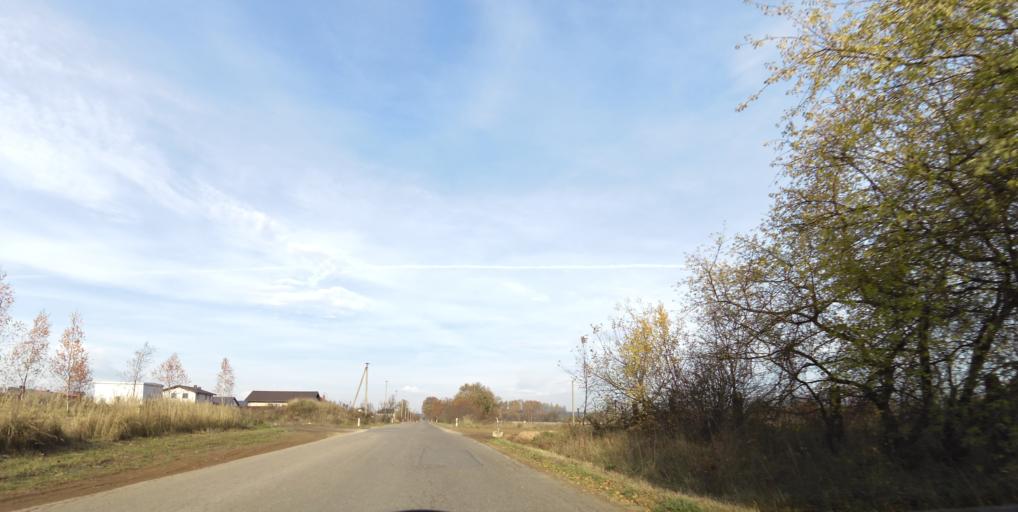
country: LT
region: Vilnius County
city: Pilaite
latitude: 54.7162
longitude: 25.1594
